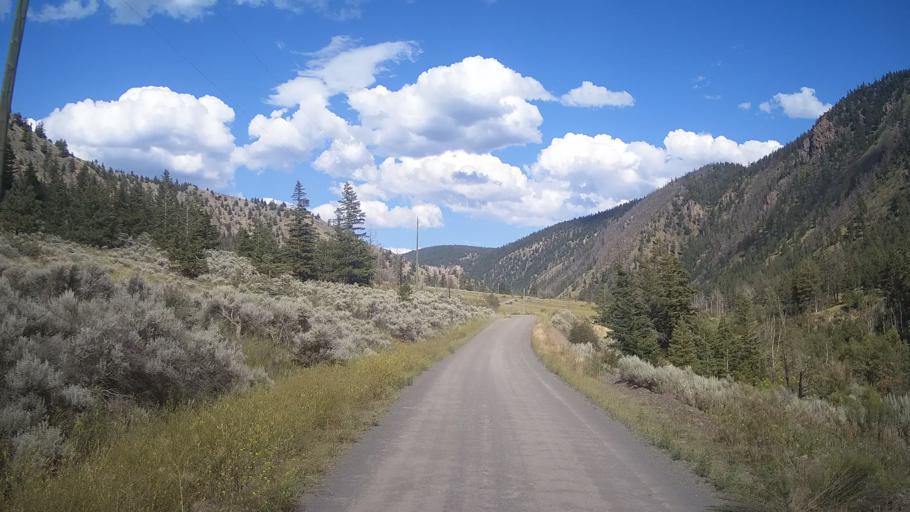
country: CA
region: British Columbia
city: Lillooet
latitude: 51.2200
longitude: -122.0909
